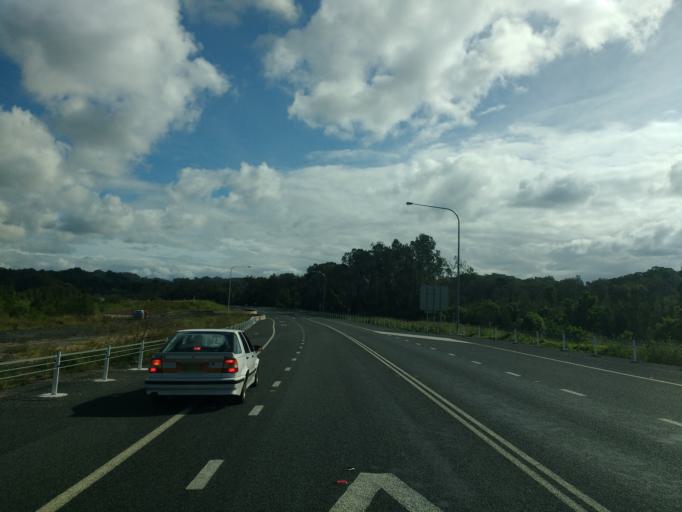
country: AU
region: New South Wales
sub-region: Ballina
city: Ballina
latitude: -28.8666
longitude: 153.4968
